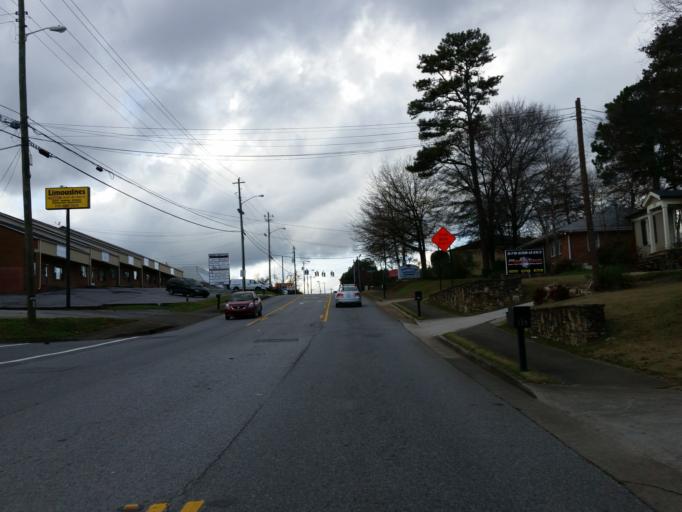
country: US
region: Georgia
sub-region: Cobb County
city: Marietta
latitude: 33.9488
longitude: -84.5077
